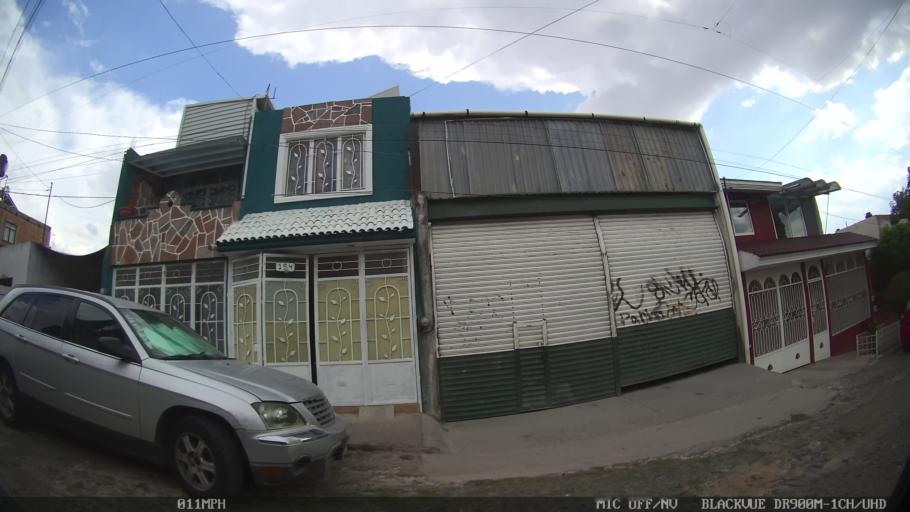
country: MX
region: Jalisco
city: Tlaquepaque
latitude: 20.6325
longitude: -103.2784
